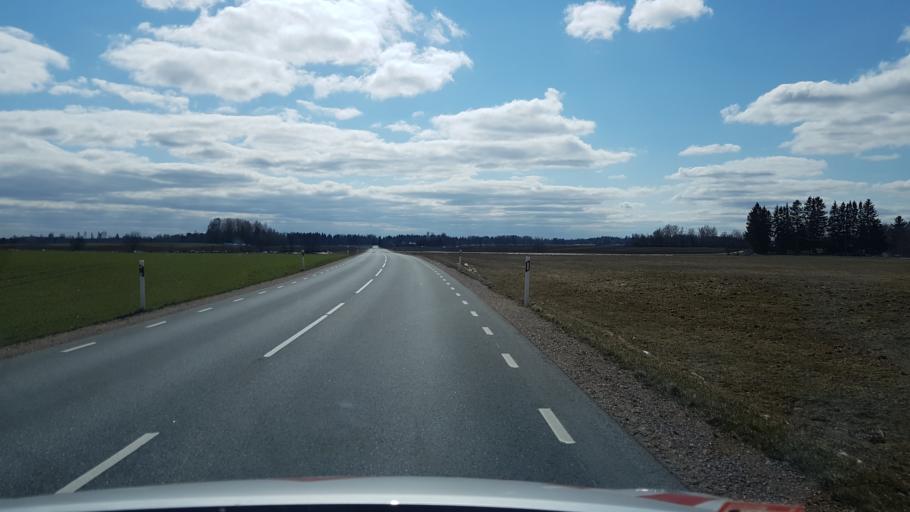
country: EE
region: Laeaene-Virumaa
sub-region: Tapa vald
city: Tapa
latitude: 59.3741
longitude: 26.0021
